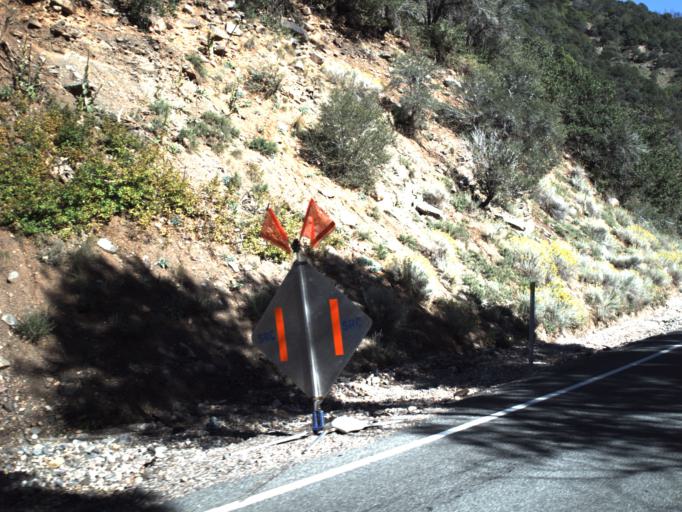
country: US
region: Utah
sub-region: Iron County
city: Parowan
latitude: 37.7570
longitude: -112.8439
